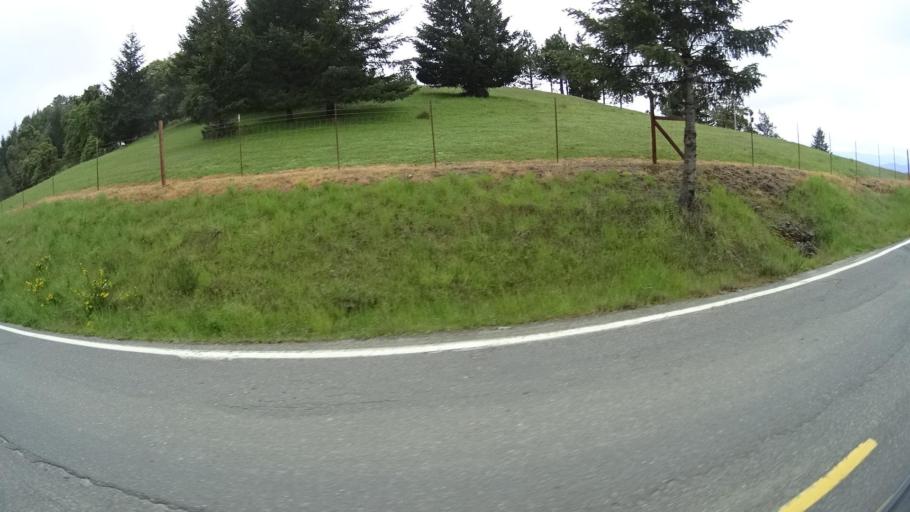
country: US
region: California
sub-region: Humboldt County
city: Redway
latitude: 40.1112
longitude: -123.7530
